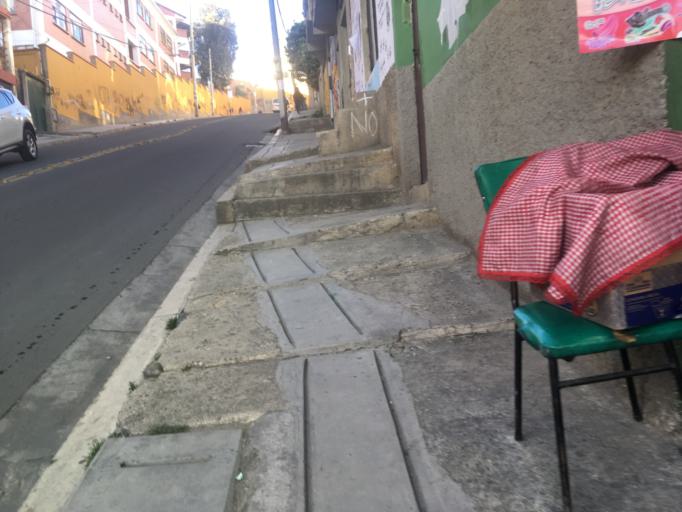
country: BO
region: La Paz
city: La Paz
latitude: -16.4989
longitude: -68.1159
